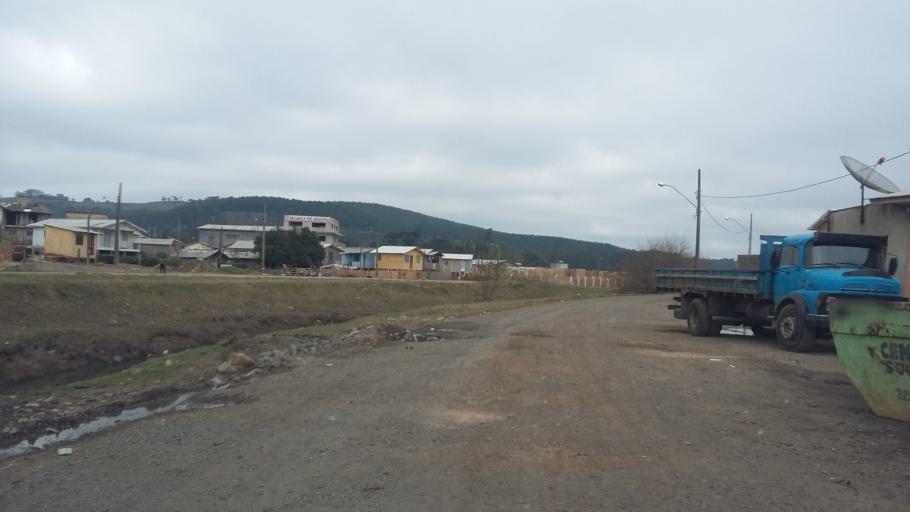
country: BR
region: Santa Catarina
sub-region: Lages
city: Lages
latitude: -27.8341
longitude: -50.3210
